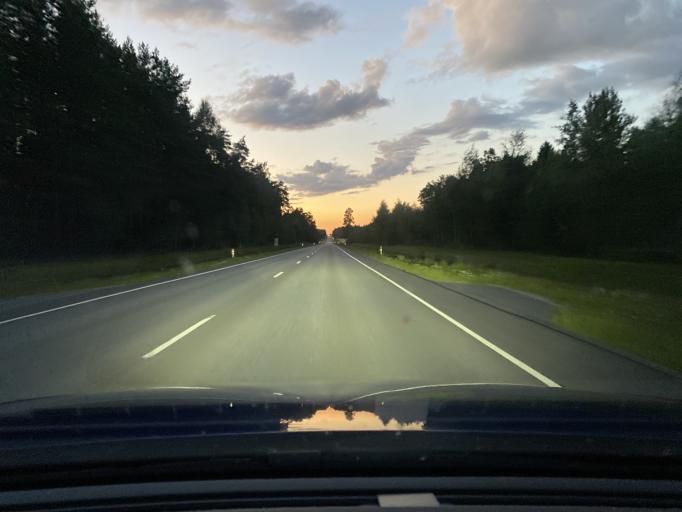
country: FI
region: Satakunta
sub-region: Pori
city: Vampula
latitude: 60.9361
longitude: 22.6830
